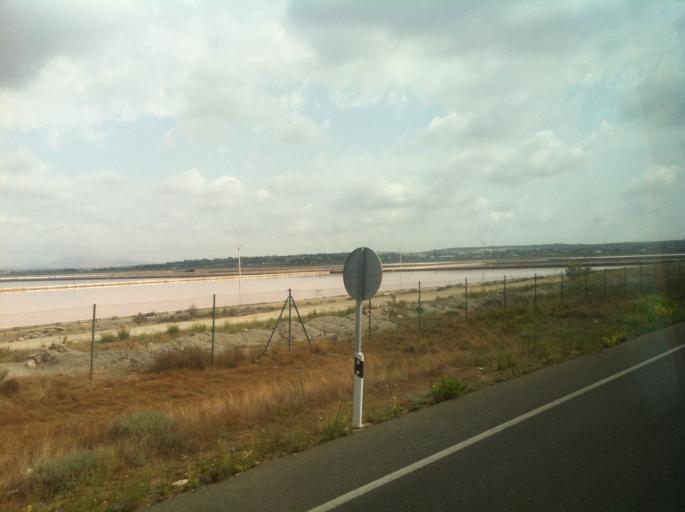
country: ES
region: Valencia
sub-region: Provincia de Alicante
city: Santa Pola
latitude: 38.1926
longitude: -0.5909
